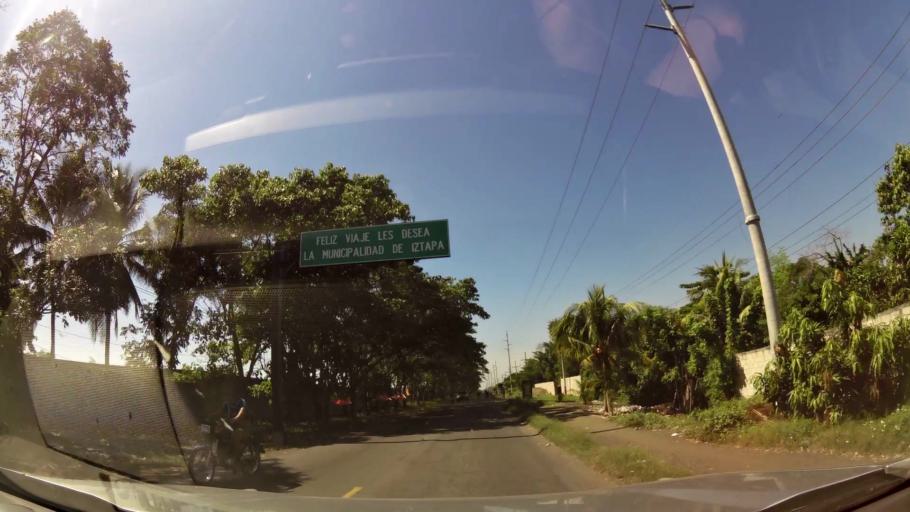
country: GT
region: Escuintla
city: Iztapa
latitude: 13.9347
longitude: -90.7532
